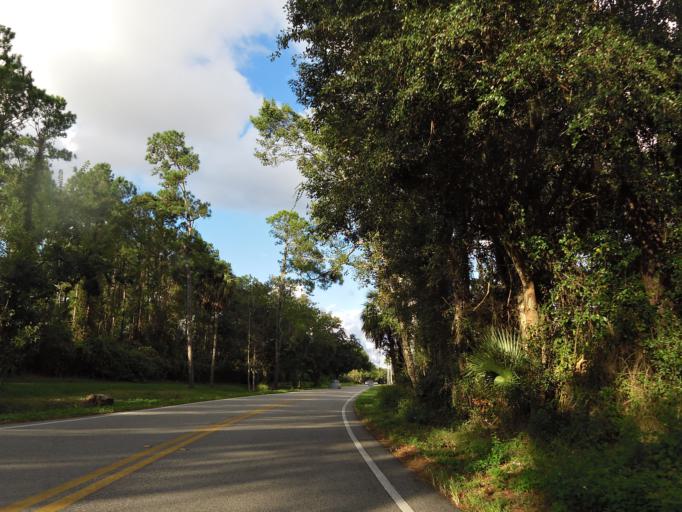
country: US
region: Florida
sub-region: Saint Johns County
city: Palm Valley
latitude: 30.1551
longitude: -81.3743
